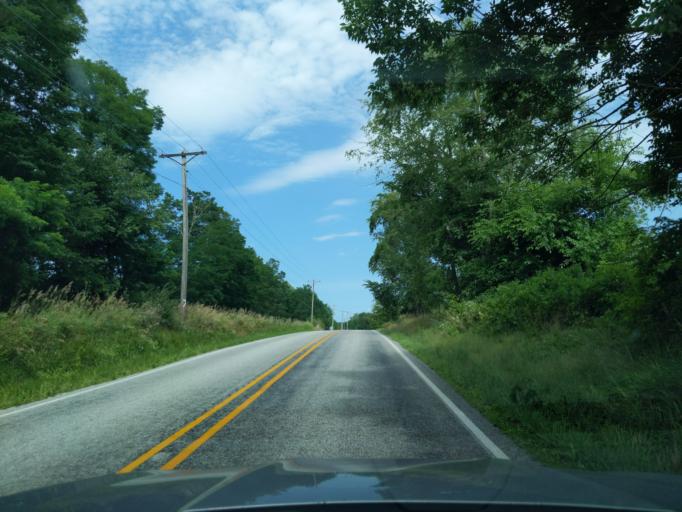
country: US
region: Indiana
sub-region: Ripley County
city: Osgood
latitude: 39.1923
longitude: -85.2187
